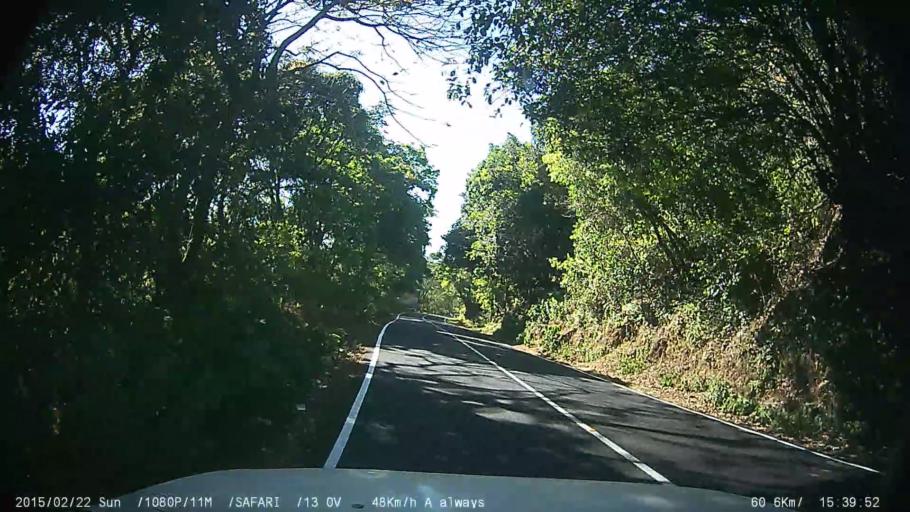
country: IN
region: Kerala
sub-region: Kottayam
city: Erattupetta
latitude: 9.5674
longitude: 76.9776
